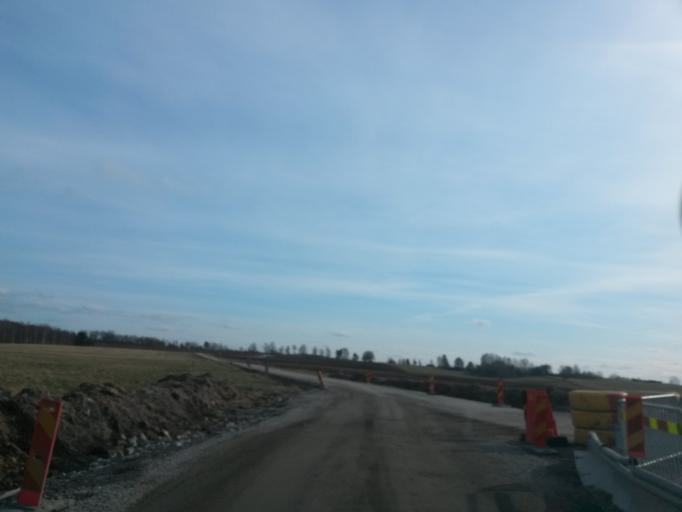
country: SE
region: Vaestra Goetaland
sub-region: Vargarda Kommun
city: Jonstorp
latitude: 57.9870
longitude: 12.6520
